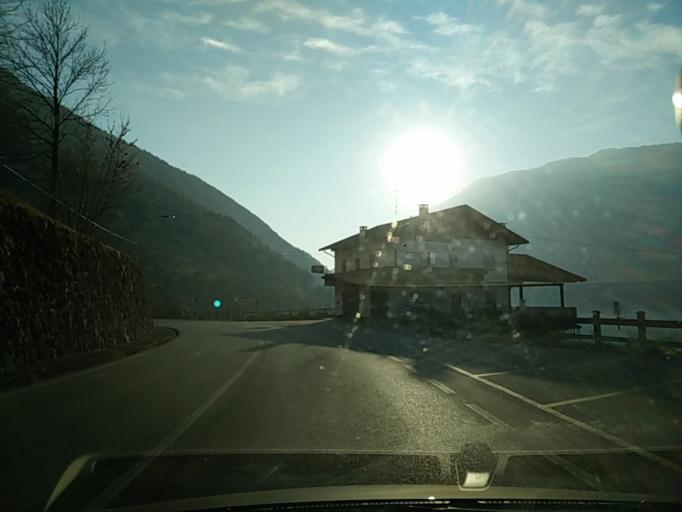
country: IT
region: Veneto
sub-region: Provincia di Belluno
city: Farra d'Alpago
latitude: 46.1083
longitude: 12.3539
